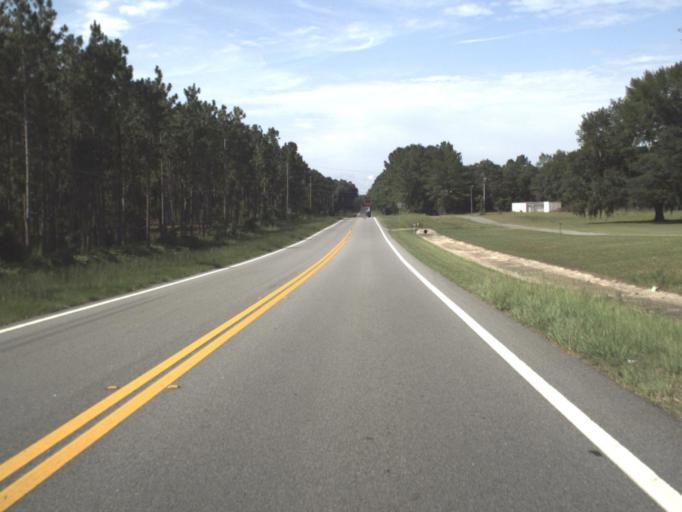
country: US
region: Florida
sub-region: Madison County
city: Madison
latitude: 30.5879
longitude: -83.3536
